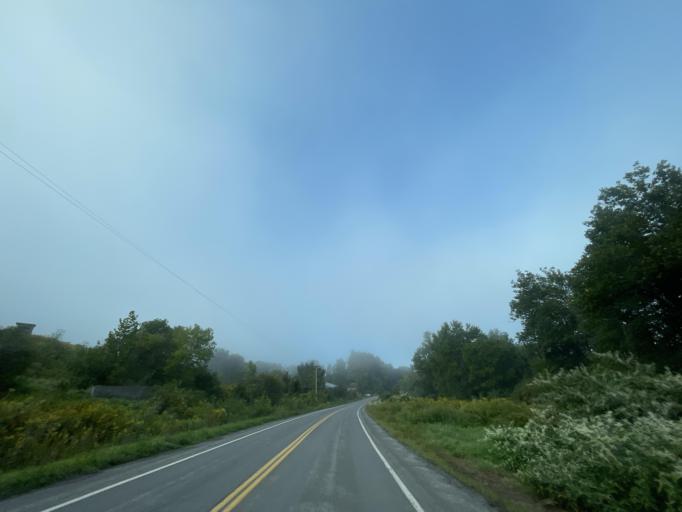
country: US
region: New York
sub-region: Chenango County
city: Oxford
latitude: 42.3690
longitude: -75.6411
